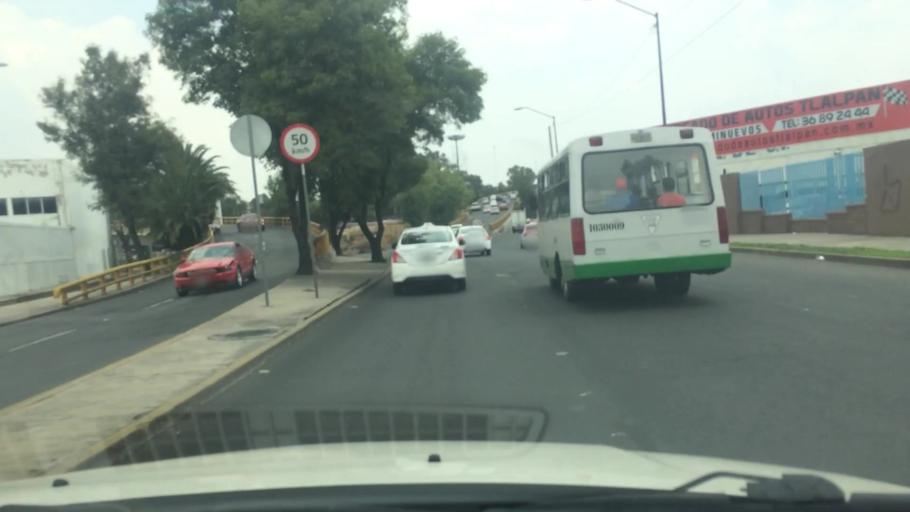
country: MX
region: Mexico City
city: Tlalpan
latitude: 19.3161
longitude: -99.1372
